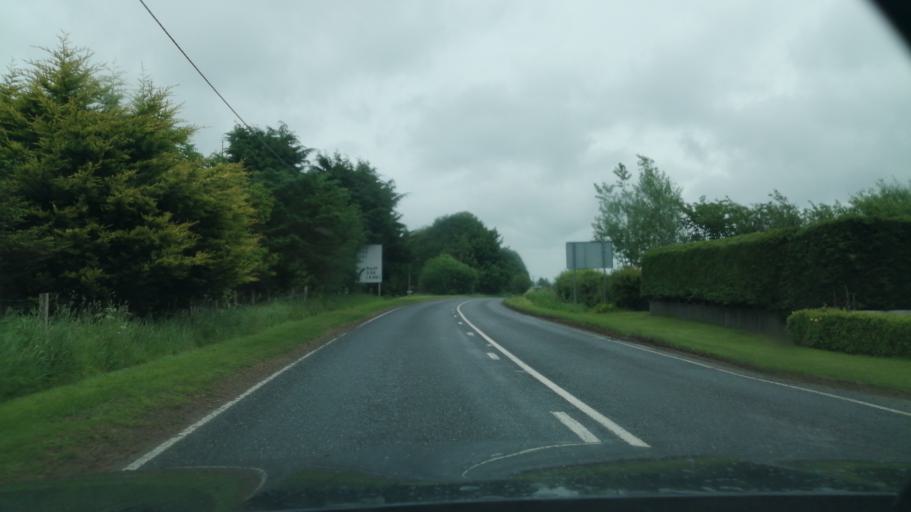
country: GB
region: Scotland
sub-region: Aberdeenshire
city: Portsoy
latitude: 57.5954
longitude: -2.7323
